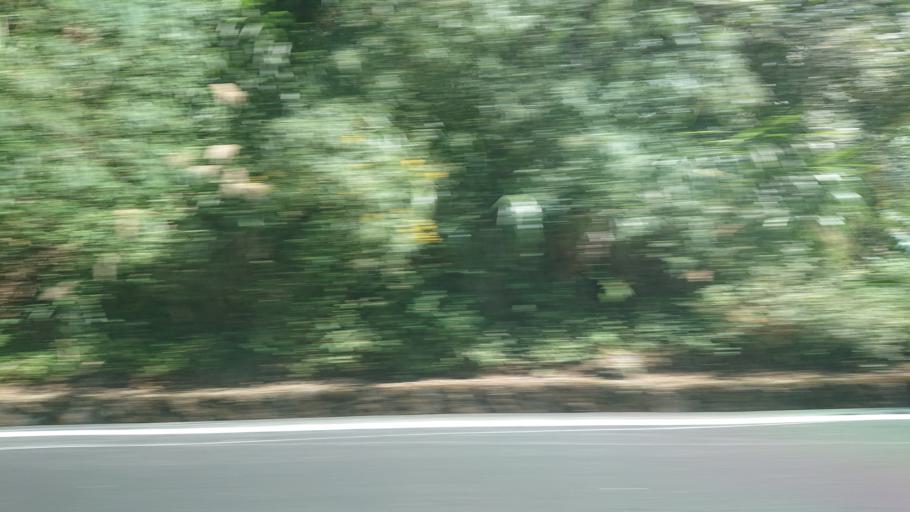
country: TW
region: Taiwan
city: Lugu
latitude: 23.4966
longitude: 120.8197
